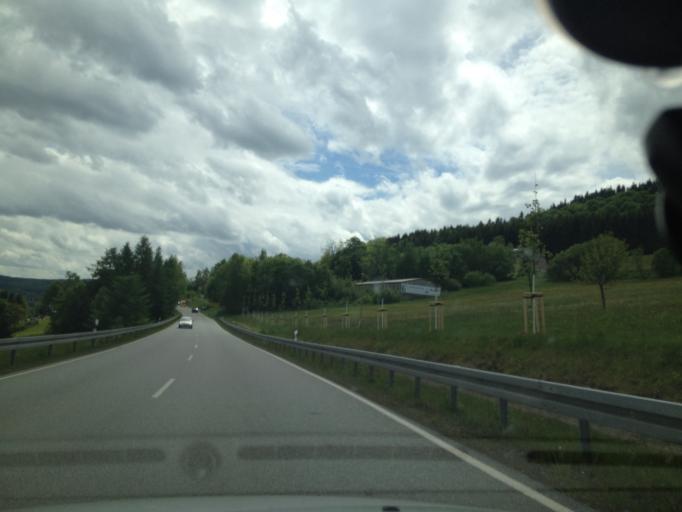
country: DE
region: Saxony
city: Barenstein
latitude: 50.5117
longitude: 13.0268
